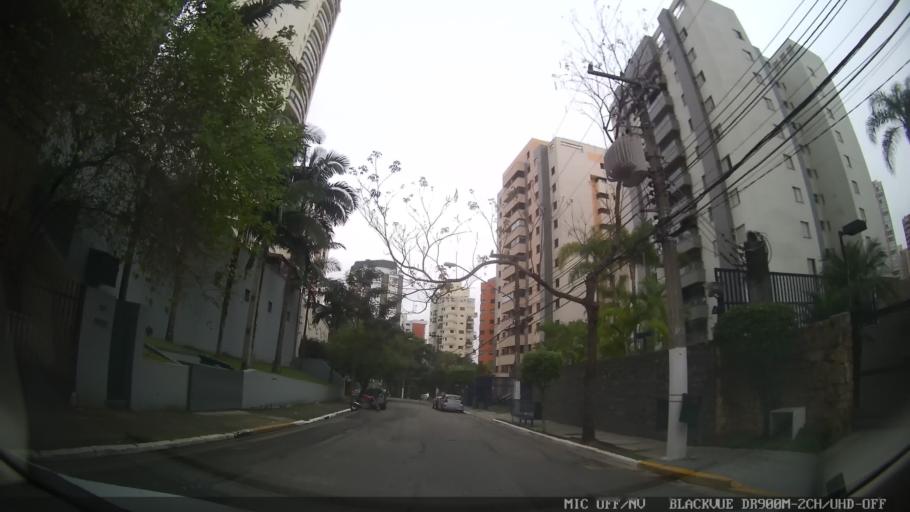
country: BR
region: Sao Paulo
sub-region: Sao Paulo
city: Sao Paulo
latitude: -23.5923
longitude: -46.6261
